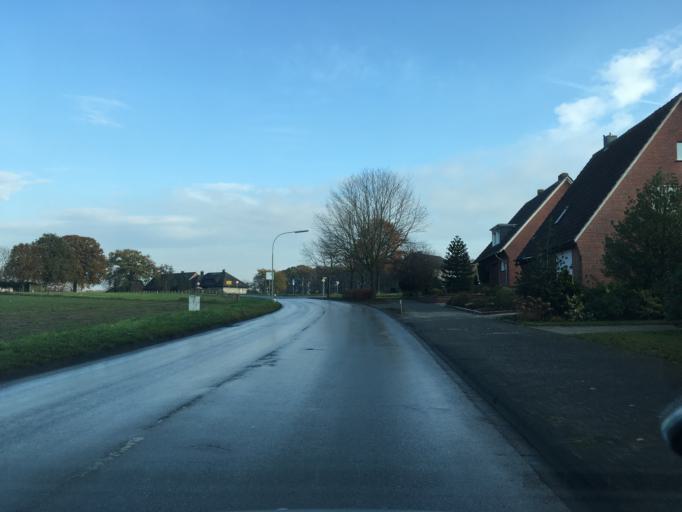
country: DE
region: North Rhine-Westphalia
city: Stadtlohn
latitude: 51.9998
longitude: 6.9345
